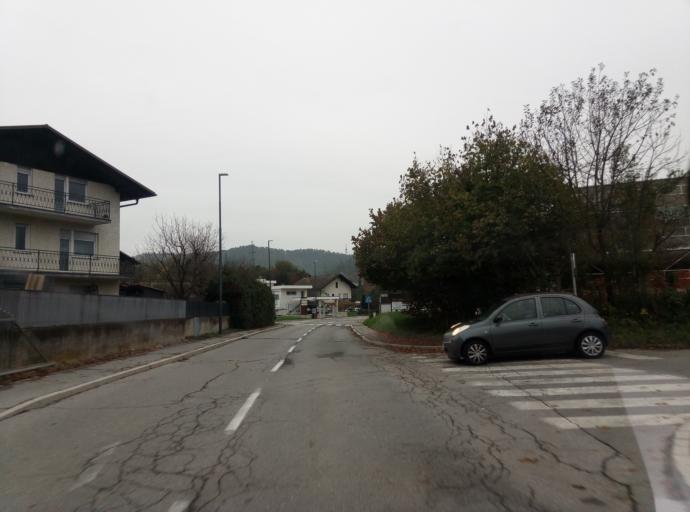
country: SI
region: Trzin
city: Trzin
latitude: 46.1080
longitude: 14.5261
